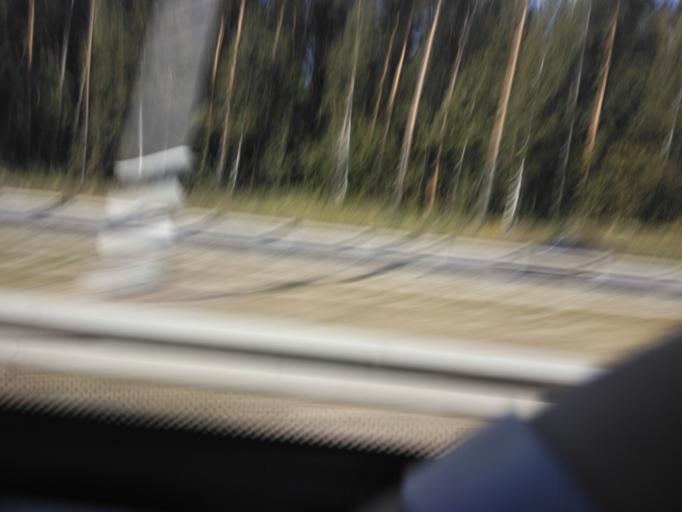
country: RU
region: Tula
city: Zaokskiy
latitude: 54.7828
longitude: 37.4881
